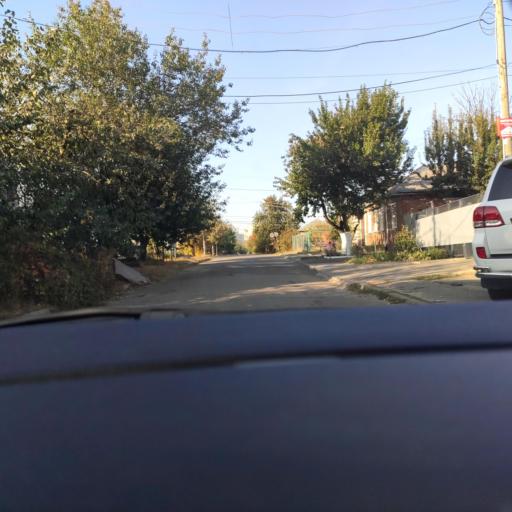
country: RU
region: Voronezj
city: Voronezh
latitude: 51.6966
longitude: 39.1619
